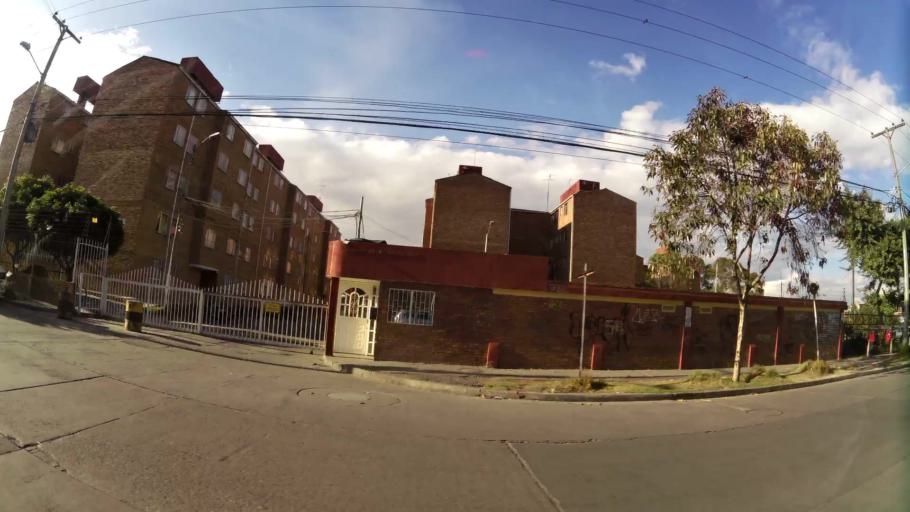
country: CO
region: Cundinamarca
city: Soacha
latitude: 4.5782
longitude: -74.1555
